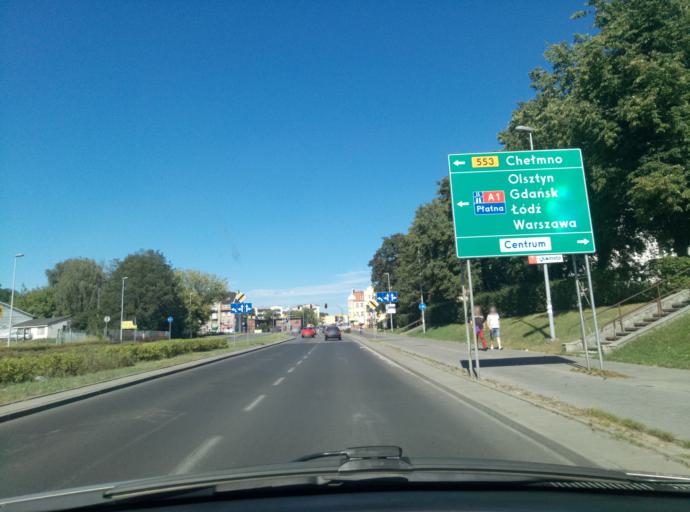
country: PL
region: Kujawsko-Pomorskie
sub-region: Torun
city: Torun
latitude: 53.0202
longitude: 18.5948
